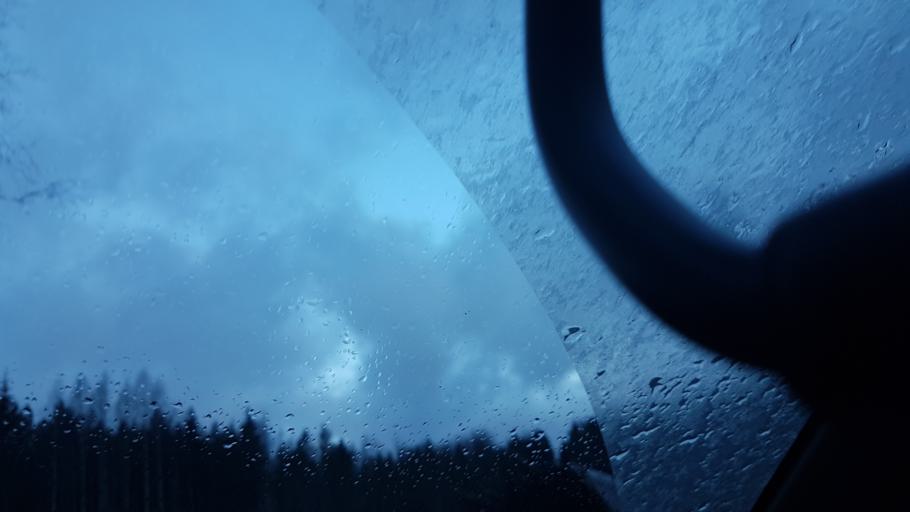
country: FI
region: Uusimaa
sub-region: Helsinki
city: Lohja
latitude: 60.2156
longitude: 24.0888
